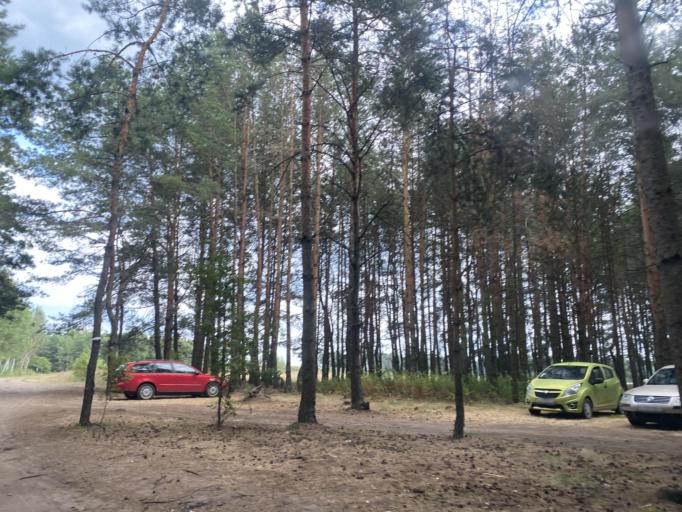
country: BY
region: Brest
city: Ivanava
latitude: 52.3665
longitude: 25.6322
